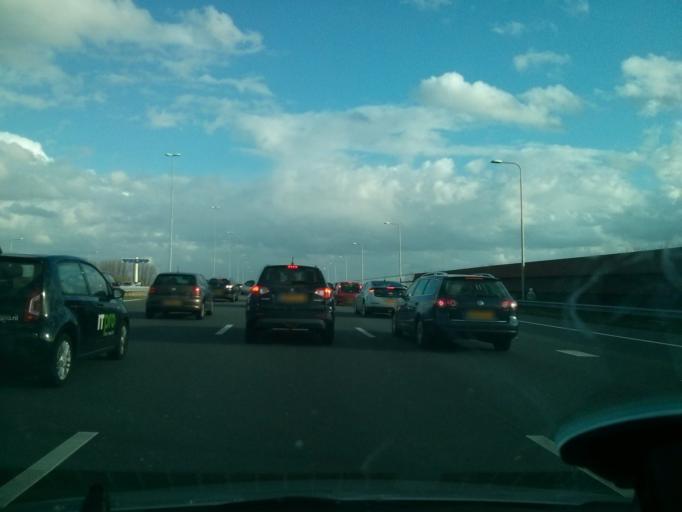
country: NL
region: Gelderland
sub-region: Gemeente Culemborg
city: Culemborg
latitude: 51.9003
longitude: 5.1889
